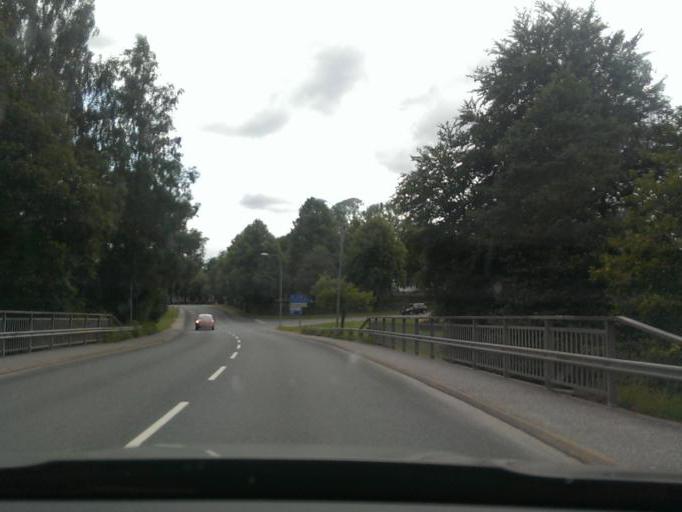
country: SE
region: Joenkoeping
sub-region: Varnamo Kommun
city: Forsheda
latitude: 57.1639
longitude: 13.8292
